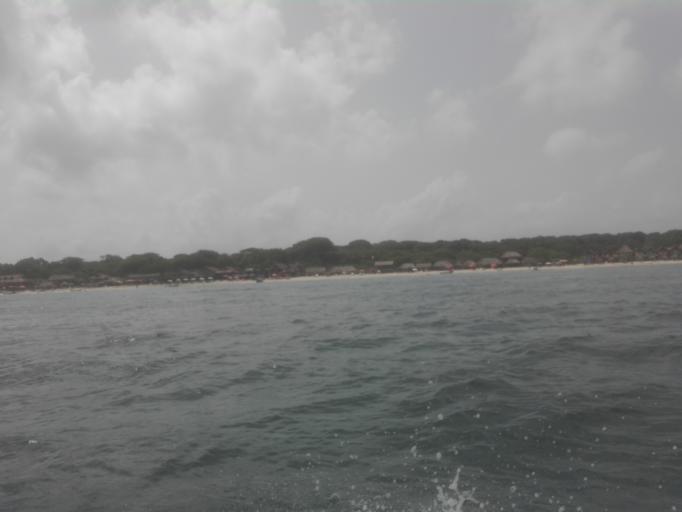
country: CO
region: Bolivar
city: Turbana
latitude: 10.2243
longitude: -75.6103
